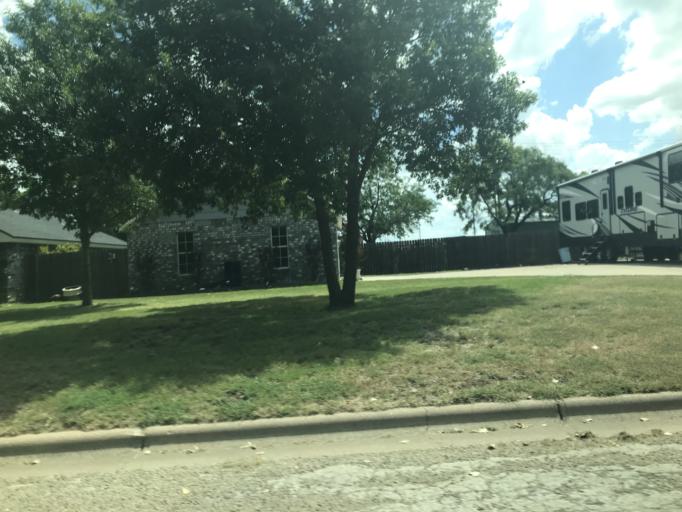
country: US
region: Texas
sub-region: Taylor County
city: Abilene
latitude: 32.4393
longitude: -99.6978
